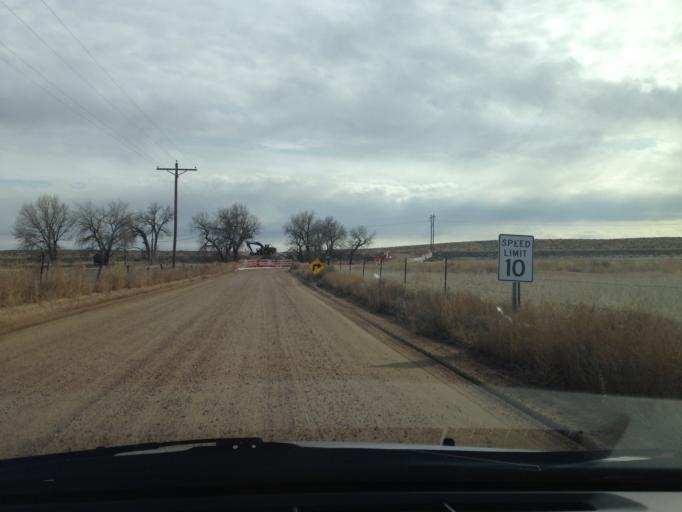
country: US
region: Colorado
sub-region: Weld County
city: Keenesburg
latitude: 40.2859
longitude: -104.2068
